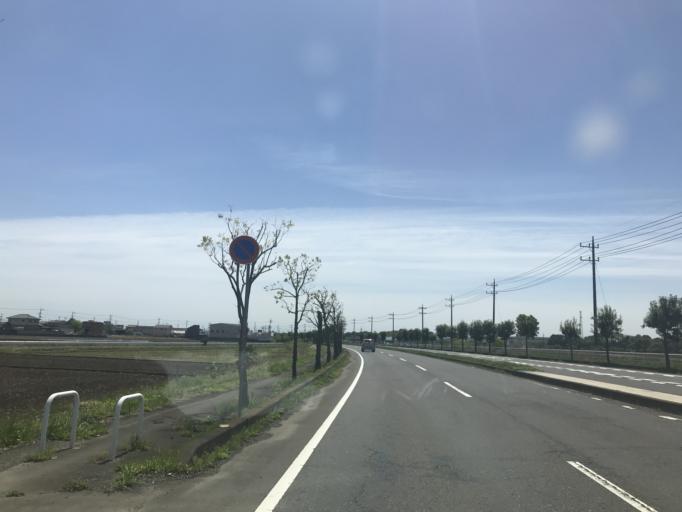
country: JP
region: Ibaraki
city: Shimodate
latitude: 36.2876
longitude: 139.9707
